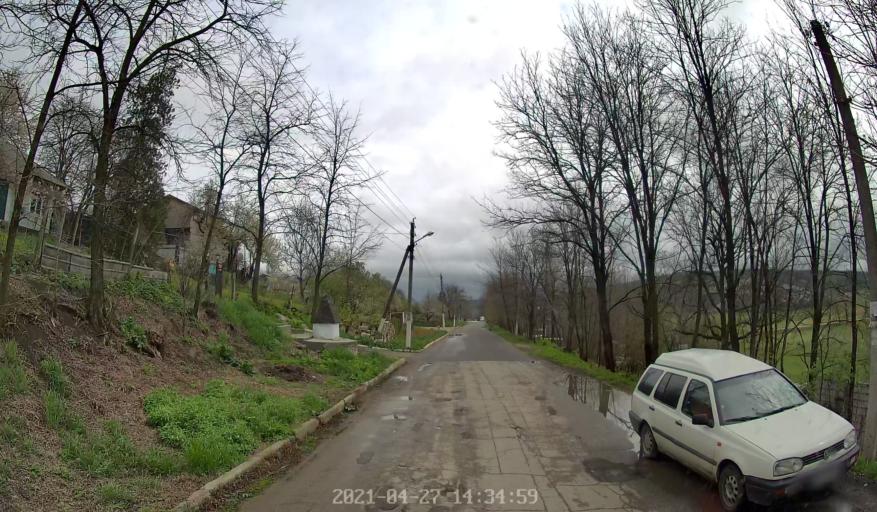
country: MD
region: Chisinau
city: Vadul lui Voda
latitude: 47.0543
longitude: 29.0346
